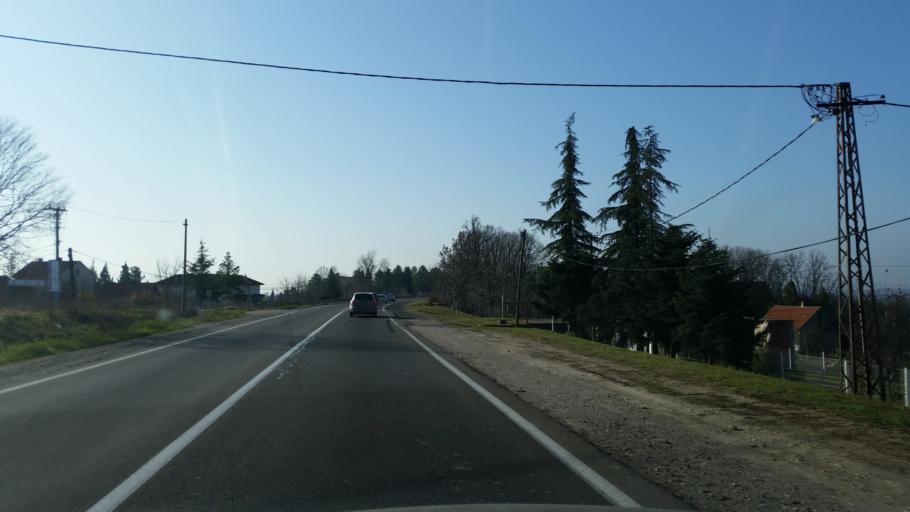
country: RS
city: Vranic
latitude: 44.5893
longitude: 20.3433
